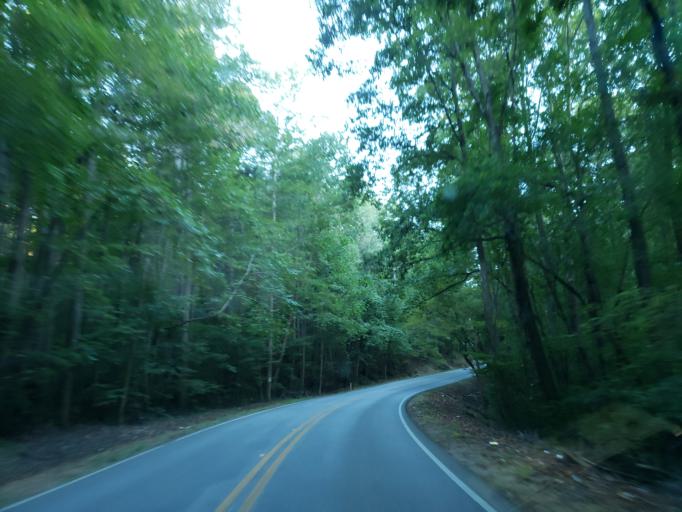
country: US
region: Georgia
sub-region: Bartow County
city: Rydal
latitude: 34.3619
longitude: -84.5803
